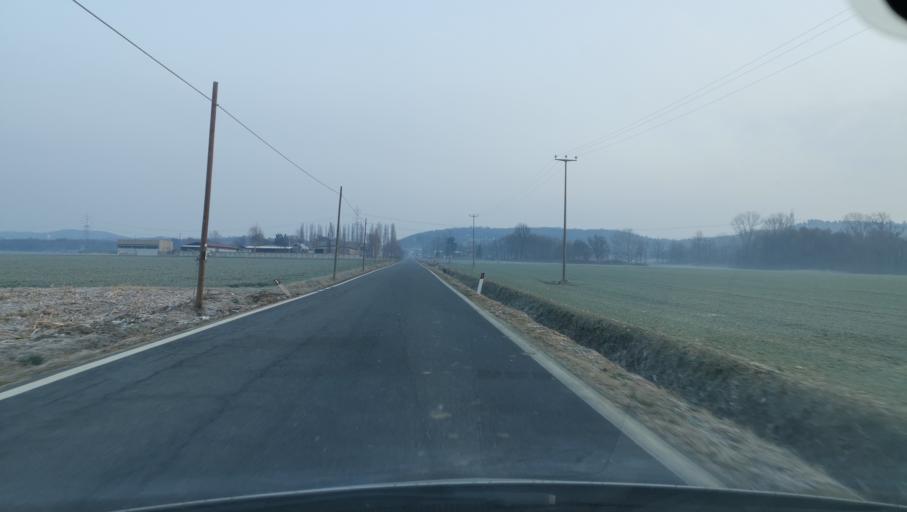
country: IT
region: Piedmont
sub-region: Provincia di Torino
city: Montalenghe
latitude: 45.3201
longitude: 7.8302
